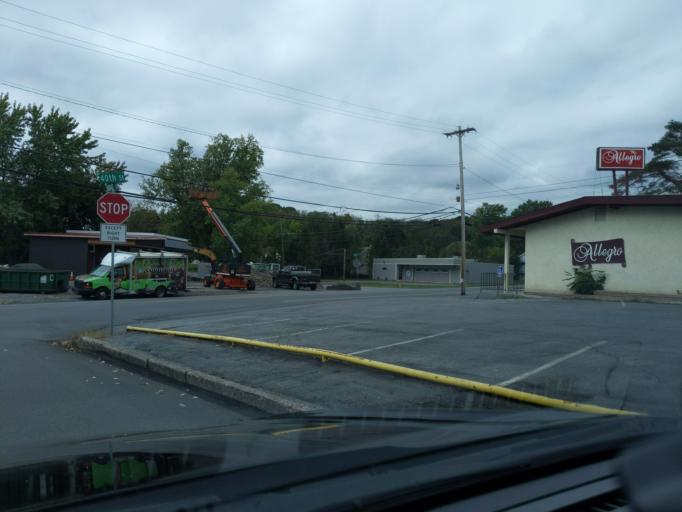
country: US
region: Pennsylvania
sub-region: Blair County
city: Lakemont
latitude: 40.4873
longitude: -78.4216
